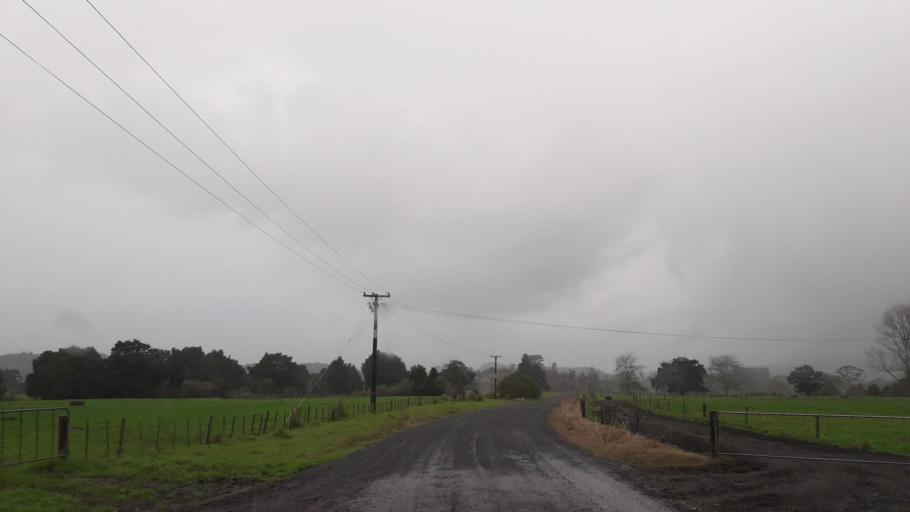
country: NZ
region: Northland
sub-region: Far North District
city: Waimate North
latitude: -35.4750
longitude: 173.6912
